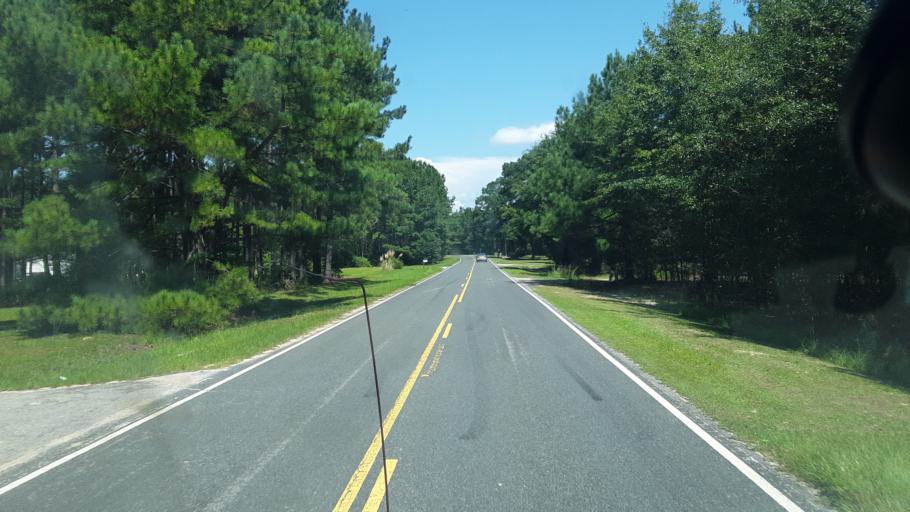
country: US
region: South Carolina
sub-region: Calhoun County
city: Oak Grove
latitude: 33.6217
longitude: -81.0133
